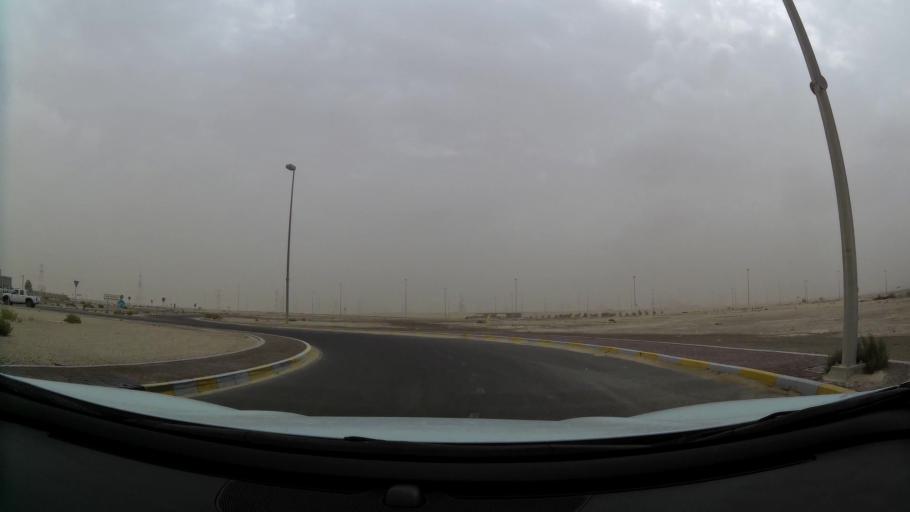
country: AE
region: Abu Dhabi
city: Abu Dhabi
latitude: 24.4219
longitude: 54.7566
